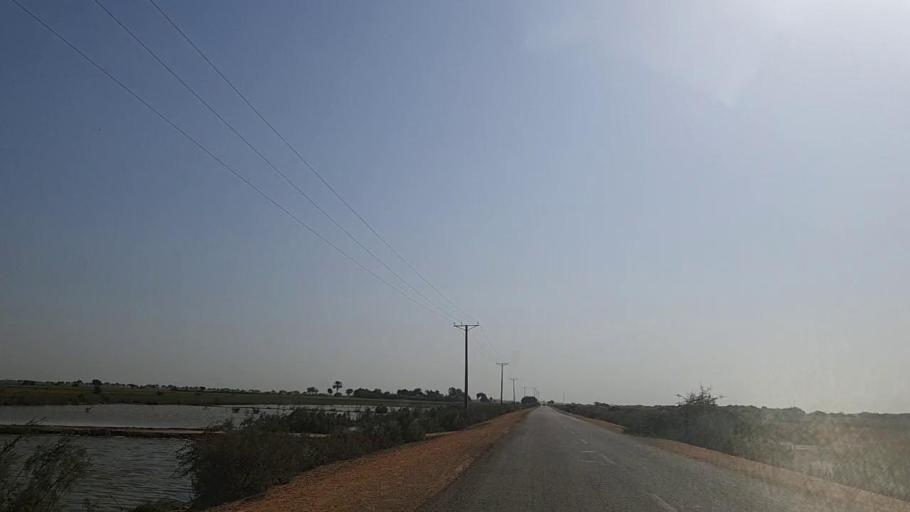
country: PK
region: Sindh
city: Mirpur Batoro
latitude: 24.5449
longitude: 68.2807
